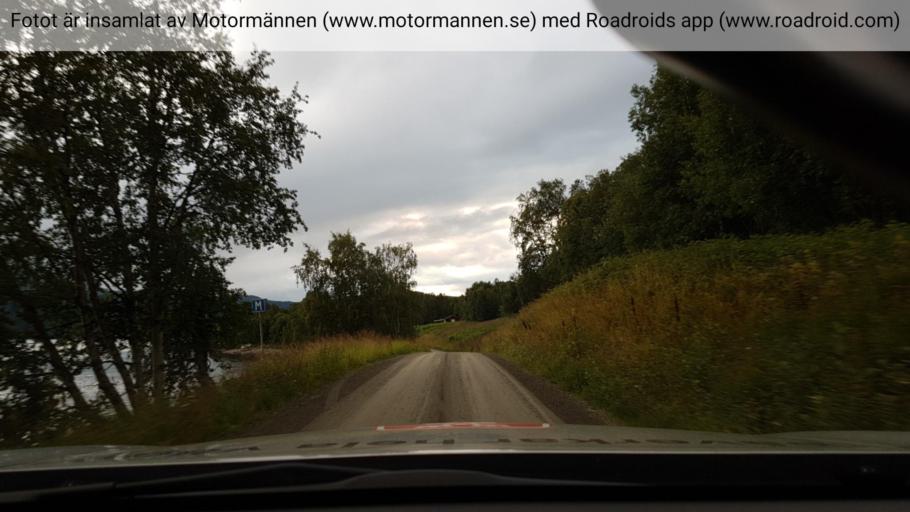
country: NO
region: Nordland
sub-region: Hattfjelldal
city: Hattfjelldal
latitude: 65.6425
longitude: 15.1978
